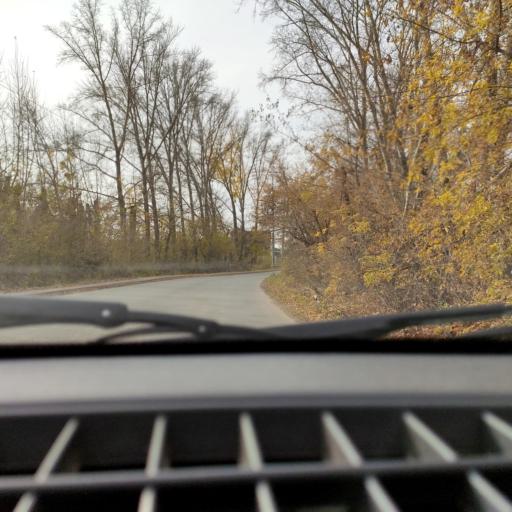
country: RU
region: Bashkortostan
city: Ufa
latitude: 54.6924
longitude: 55.9660
